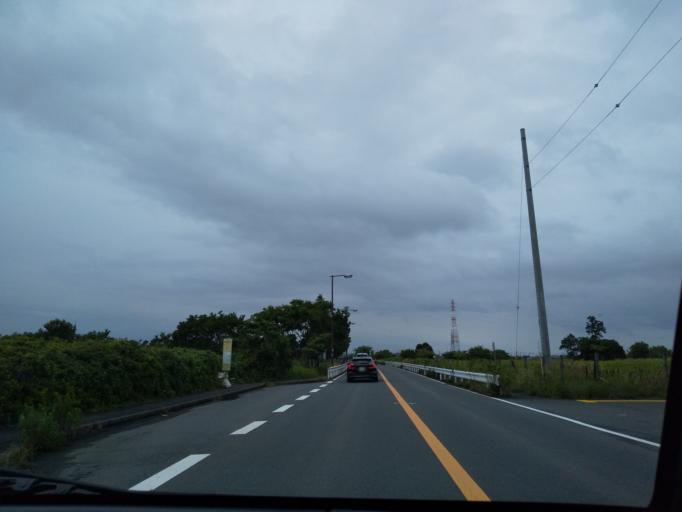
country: JP
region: Kanagawa
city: Fujisawa
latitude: 35.3980
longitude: 139.5039
